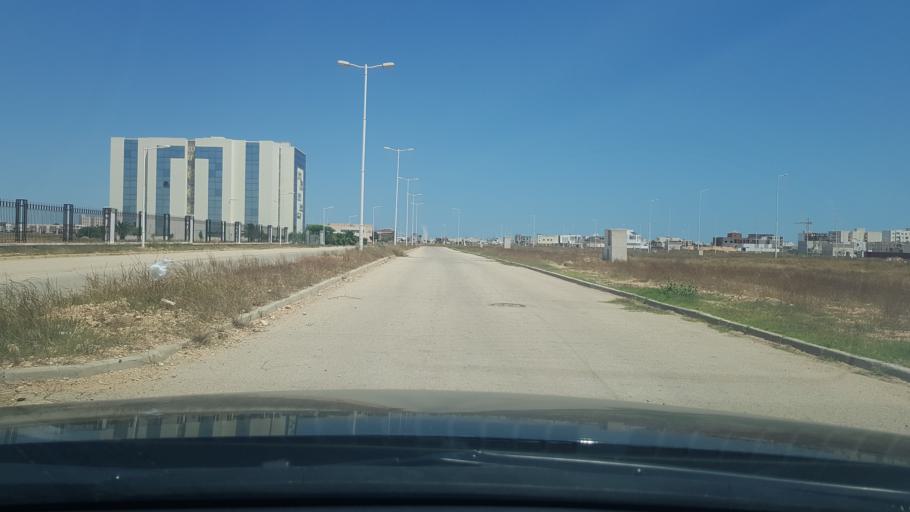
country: TN
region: Safaqis
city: Al Qarmadah
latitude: 34.8334
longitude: 10.7507
